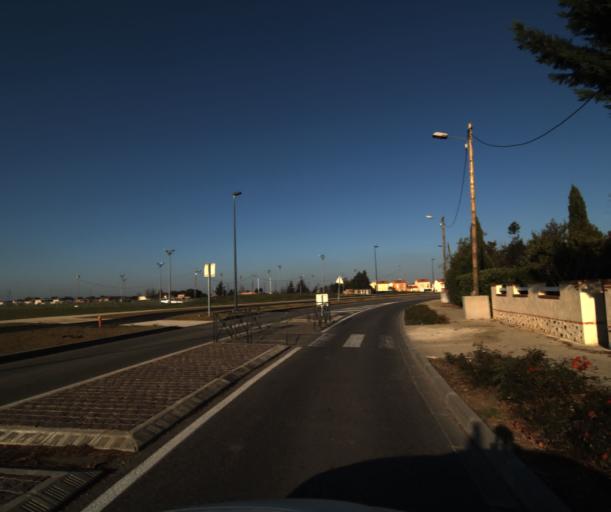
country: FR
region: Midi-Pyrenees
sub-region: Departement de la Haute-Garonne
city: Colomiers
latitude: 43.6221
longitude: 1.3210
